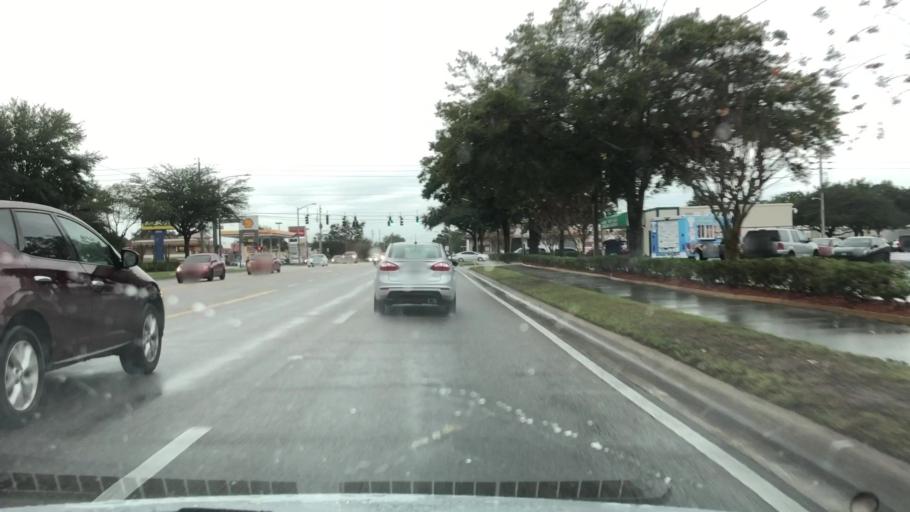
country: US
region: Florida
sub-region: Orange County
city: Conway
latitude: 28.5243
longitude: -81.3423
